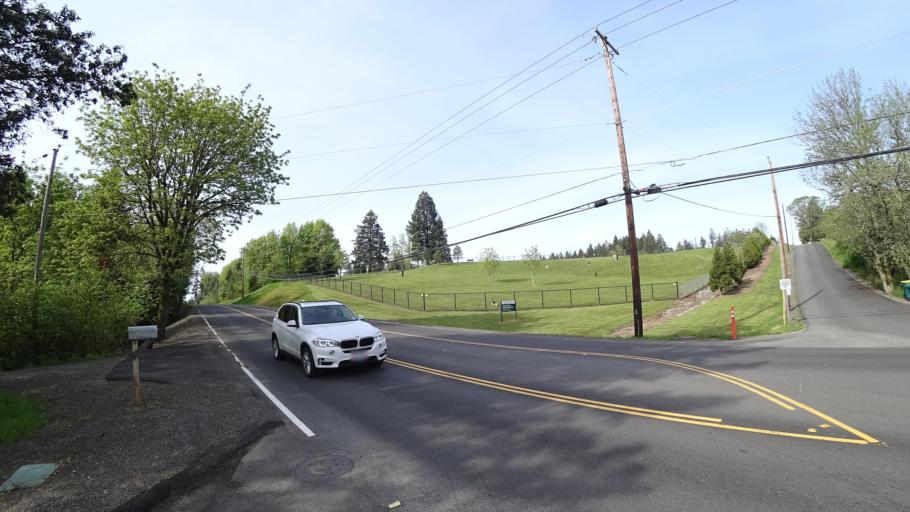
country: US
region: Oregon
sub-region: Washington County
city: Aloha
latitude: 45.4476
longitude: -122.8567
